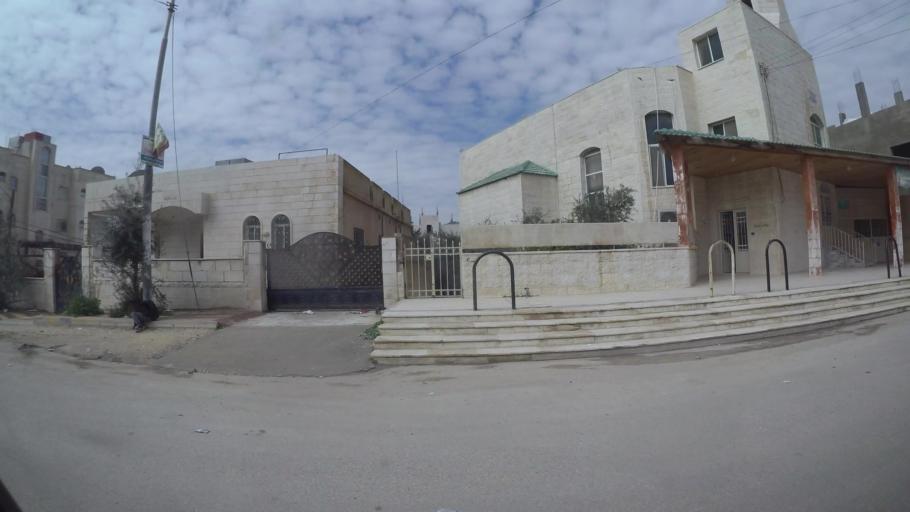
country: JO
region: Amman
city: Al Jubayhah
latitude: 32.0650
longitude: 35.8301
